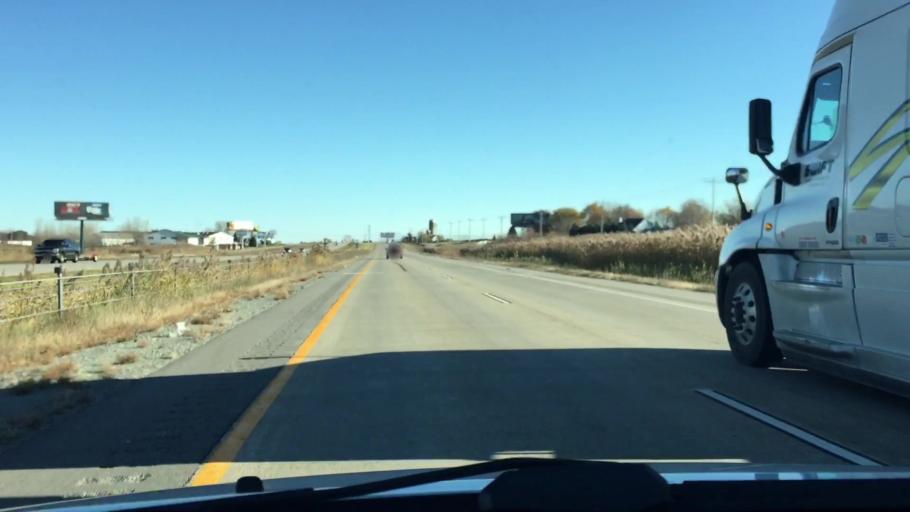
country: US
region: Wisconsin
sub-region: Brown County
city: Wrightstown
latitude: 44.3179
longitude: -88.2230
